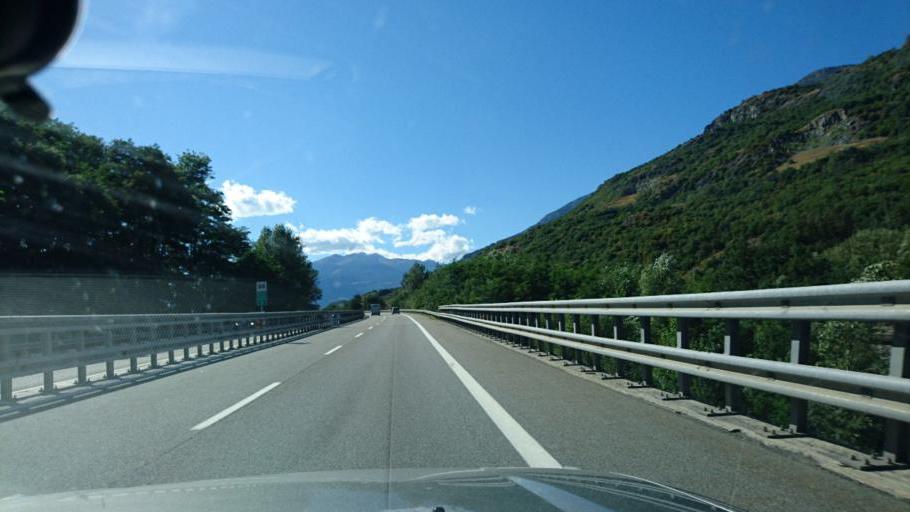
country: IT
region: Aosta Valley
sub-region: Valle d'Aosta
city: Saint Marcel
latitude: 45.7377
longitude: 7.4540
